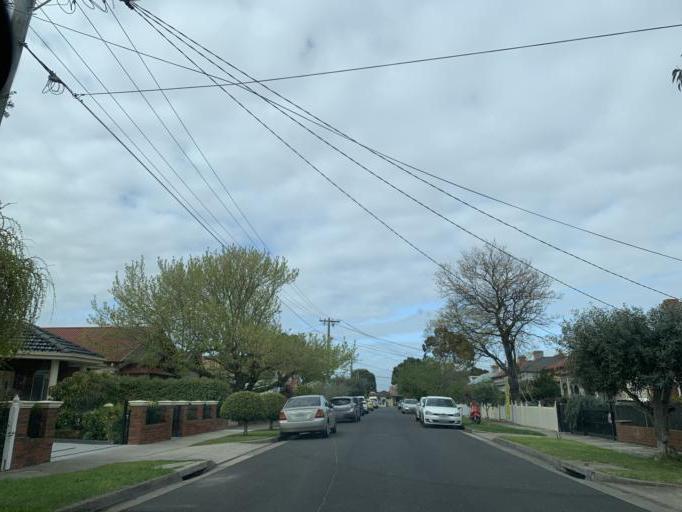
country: AU
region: Victoria
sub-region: Moreland
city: Coburg North
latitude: -37.7376
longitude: 144.9603
